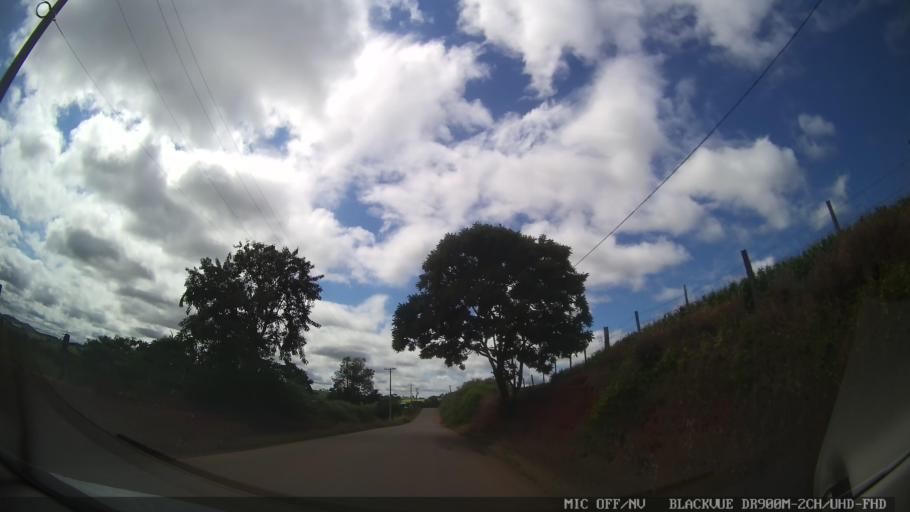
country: BR
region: Sao Paulo
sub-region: Amparo
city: Amparo
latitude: -22.8645
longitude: -46.7454
